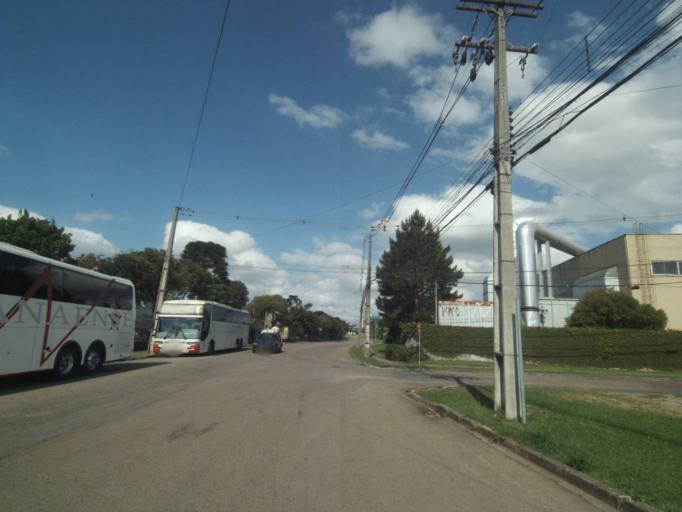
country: BR
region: Parana
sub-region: Curitiba
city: Curitiba
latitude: -25.4955
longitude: -49.3129
